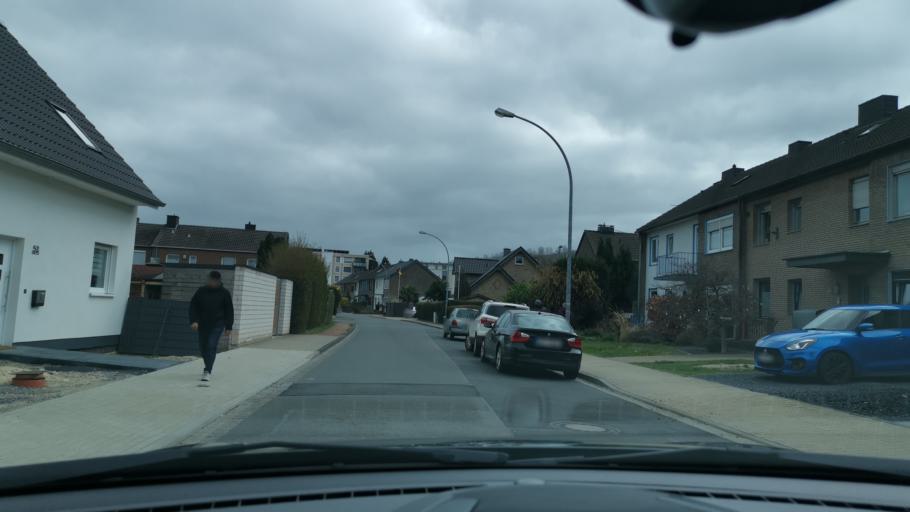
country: DE
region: North Rhine-Westphalia
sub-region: Regierungsbezirk Dusseldorf
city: Grevenbroich
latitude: 51.0809
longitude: 6.6077
